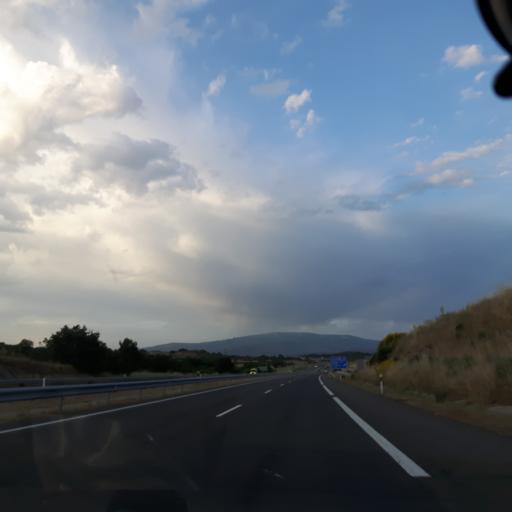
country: ES
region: Castille and Leon
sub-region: Provincia de Salamanca
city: Fuentes de Bejar
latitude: 40.5132
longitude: -5.6741
